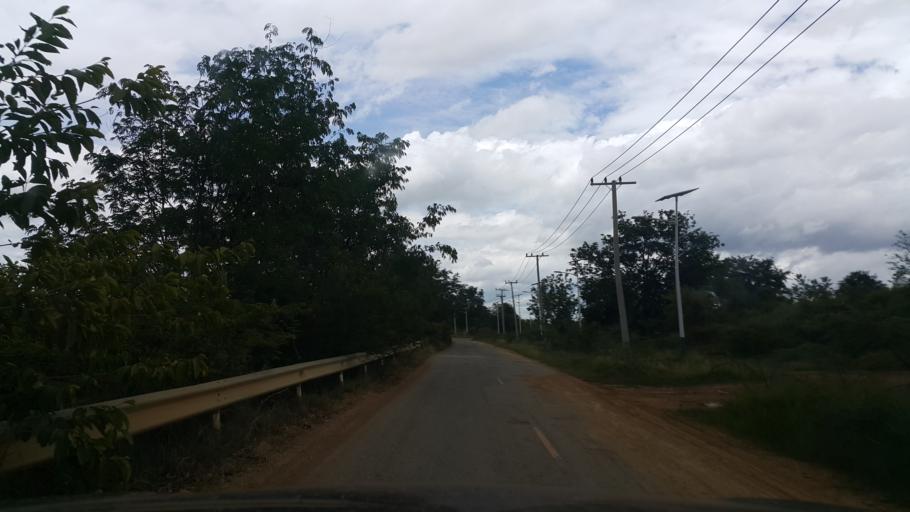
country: TH
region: Sukhothai
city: Ban Na
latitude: 17.0586
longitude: 99.7757
